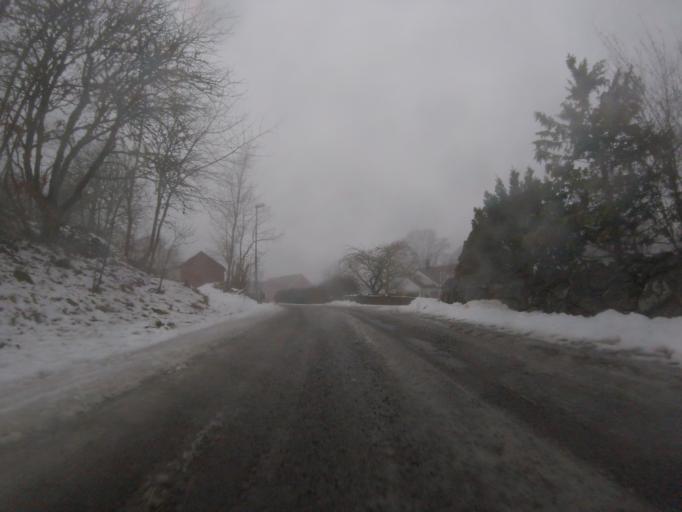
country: SE
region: Halland
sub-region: Varbergs Kommun
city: Varberg
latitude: 57.1920
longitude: 12.2155
